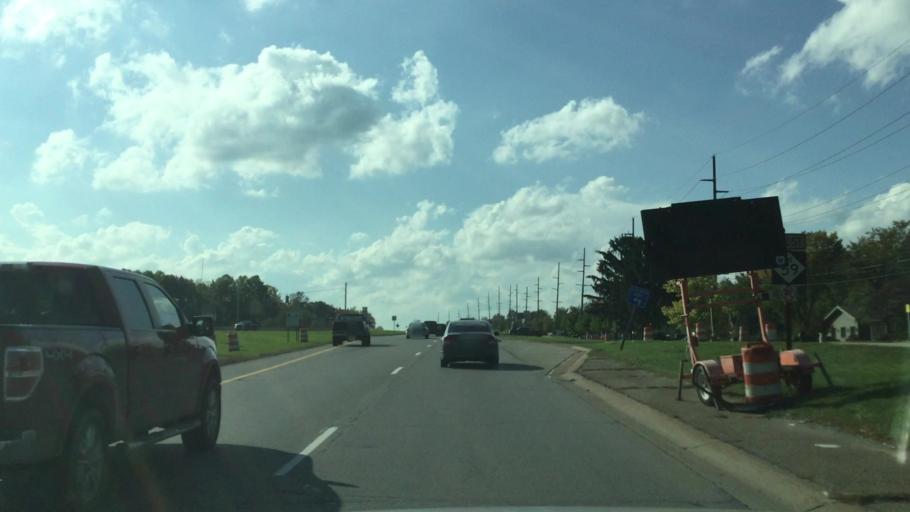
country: US
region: Michigan
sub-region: Oakland County
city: Milford
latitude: 42.6419
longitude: -83.6180
